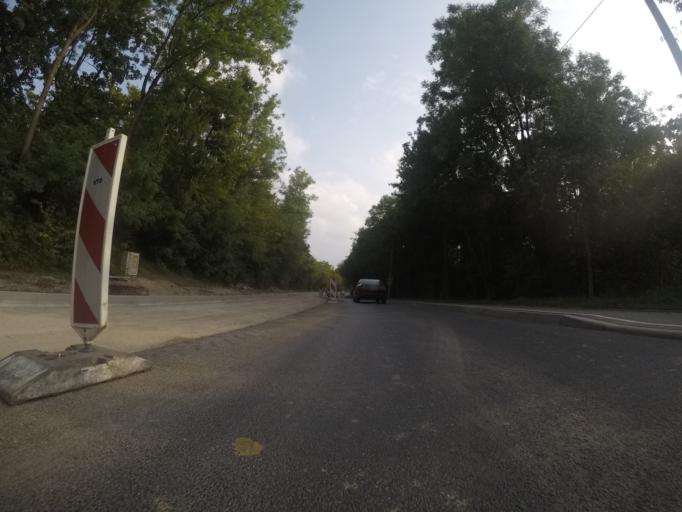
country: DE
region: Baden-Wuerttemberg
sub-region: Regierungsbezirk Stuttgart
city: Stuttgart Feuerbach
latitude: 48.7906
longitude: 9.1516
